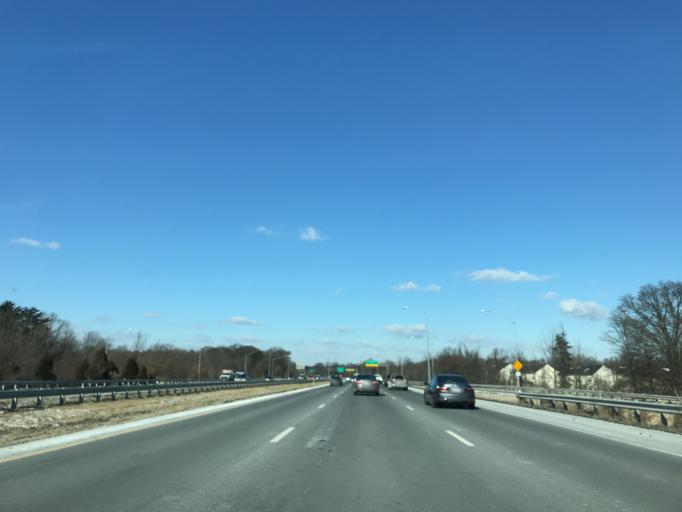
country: US
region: Maryland
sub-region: Prince George's County
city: Camp Springs
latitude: 38.8070
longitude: -76.9072
